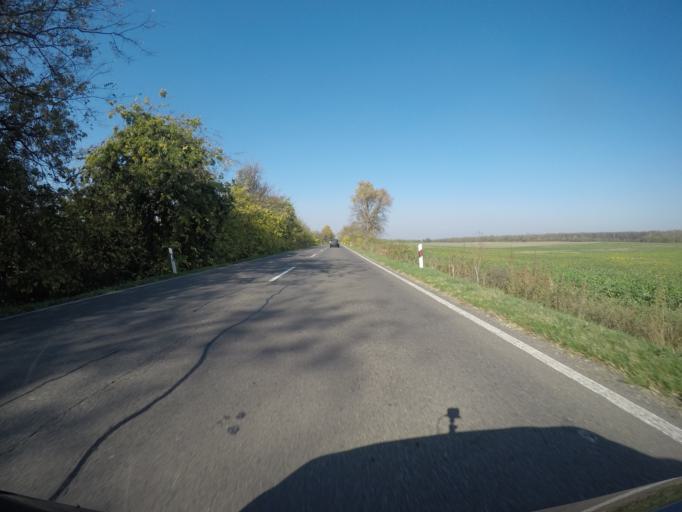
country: HU
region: Tolna
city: Tengelic
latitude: 46.5261
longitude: 18.6589
